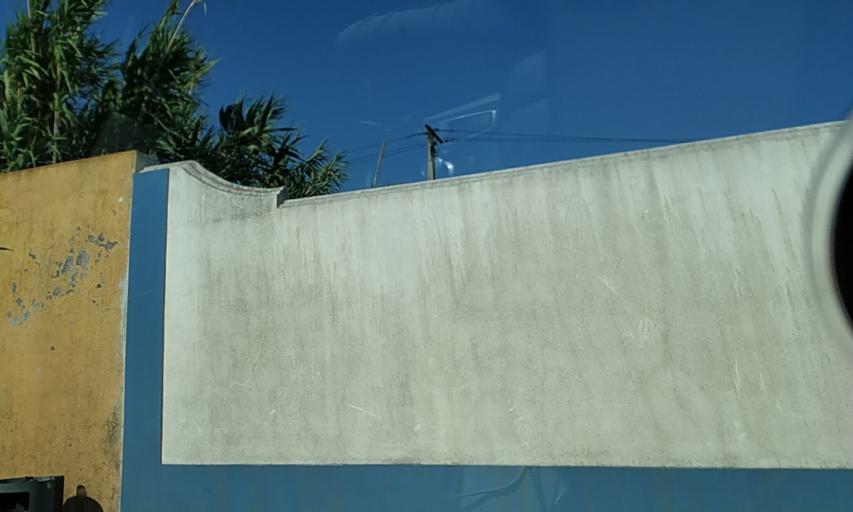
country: PT
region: Santarem
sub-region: Coruche
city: Coruche
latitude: 38.9673
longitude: -8.5354
